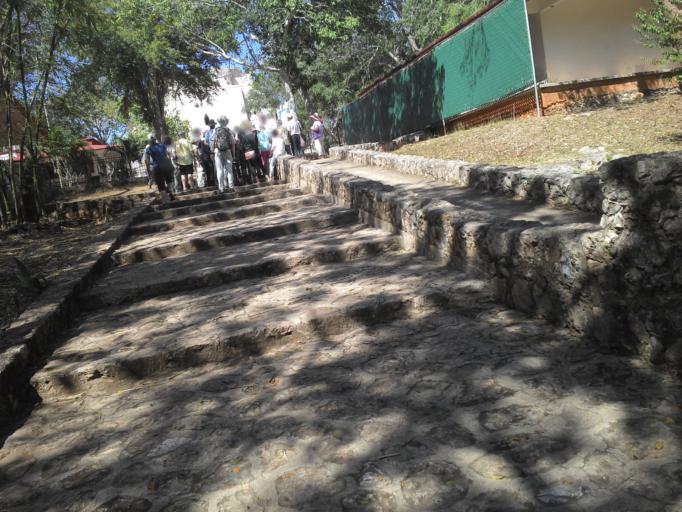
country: MX
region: Yucatan
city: Santa Elena
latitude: 20.3606
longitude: -89.7684
